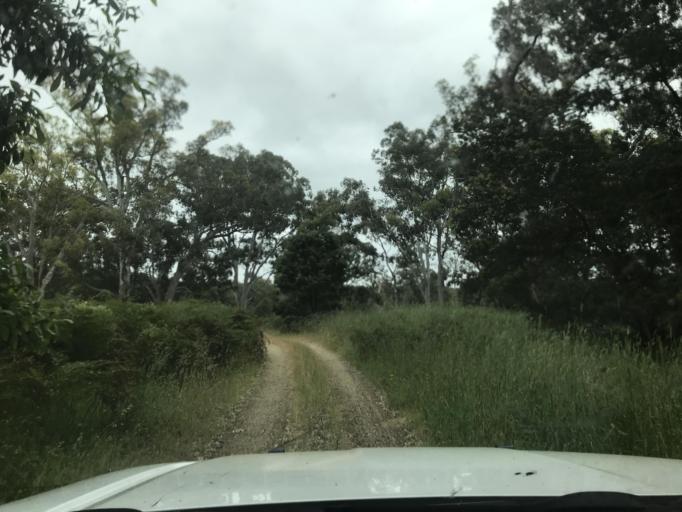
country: AU
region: South Australia
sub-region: Wattle Range
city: Penola
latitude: -37.1938
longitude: 140.9724
